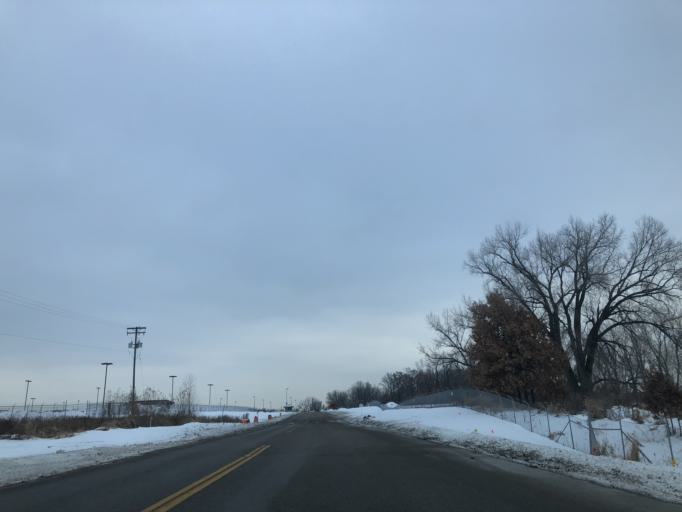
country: US
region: Minnesota
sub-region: Ramsey County
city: Shoreview
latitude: 45.0809
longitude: -93.1575
